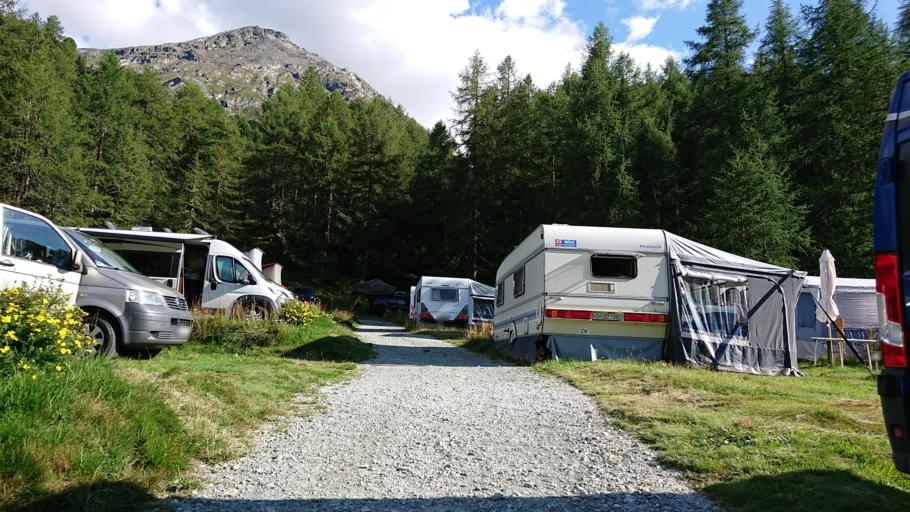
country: CH
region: Grisons
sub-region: Maloja District
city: Silvaplana
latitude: 46.4052
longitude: 9.7104
